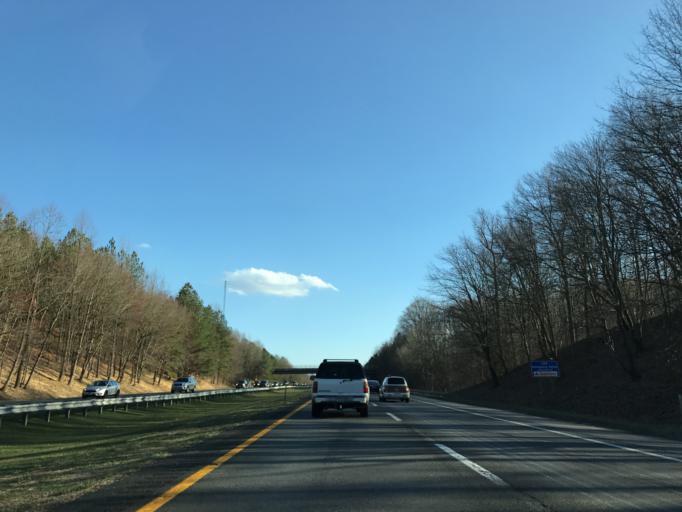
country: US
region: Maryland
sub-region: Anne Arundel County
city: Crownsville
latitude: 39.0212
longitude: -76.6149
